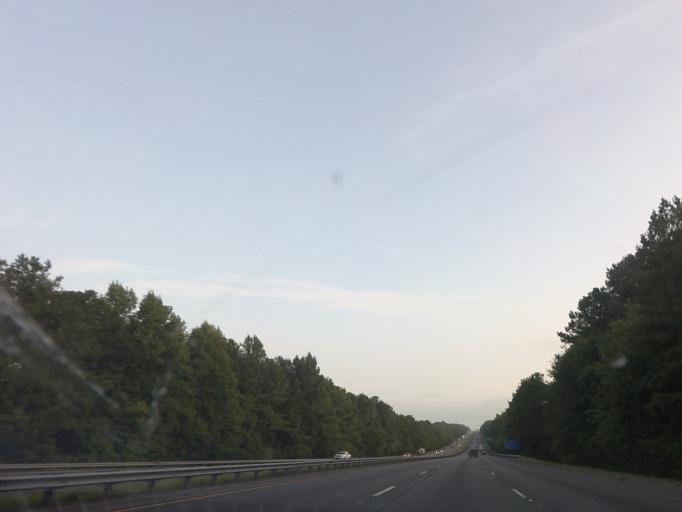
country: US
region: Georgia
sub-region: Butts County
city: Indian Springs
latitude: 33.1479
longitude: -84.0309
